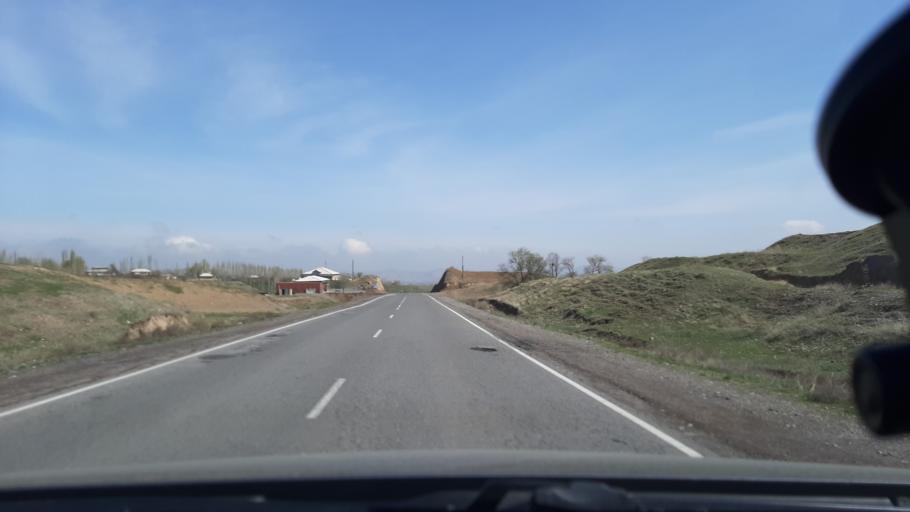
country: TJ
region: Viloyati Sughd
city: Shahriston
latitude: 39.7729
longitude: 68.8261
